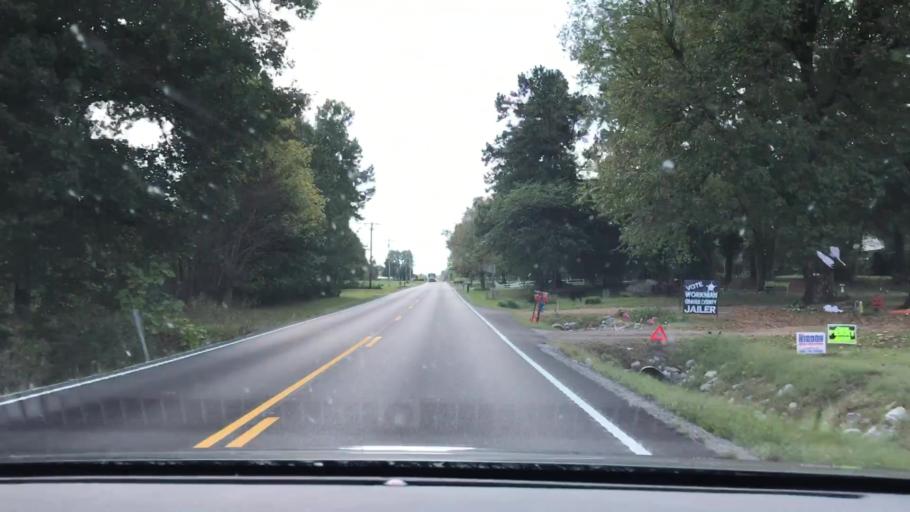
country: US
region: Kentucky
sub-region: Graves County
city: Mayfield
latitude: 36.7691
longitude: -88.5960
